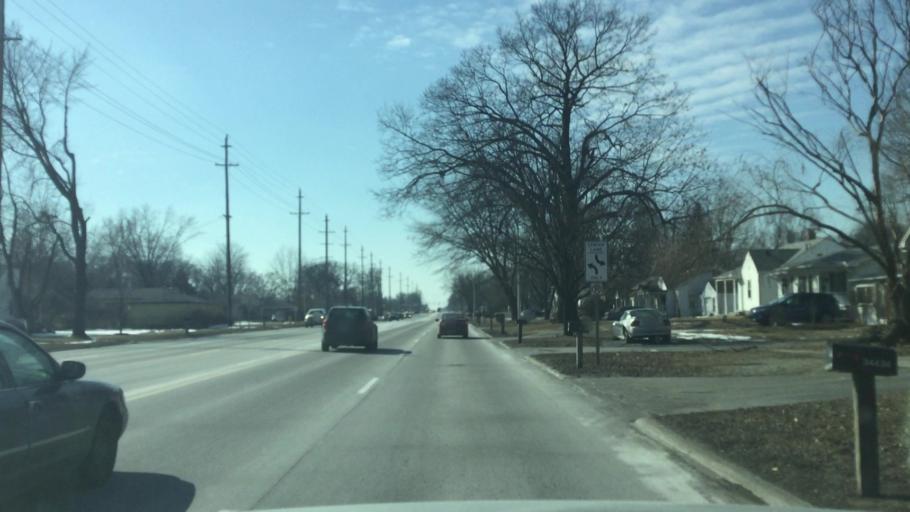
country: US
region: Michigan
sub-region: Wayne County
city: Westland
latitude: 42.3101
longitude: -83.3797
